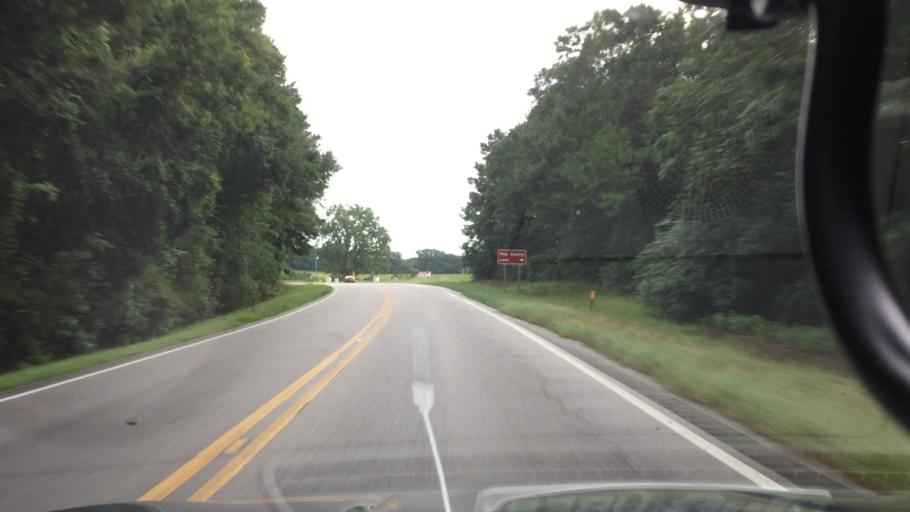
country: US
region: Alabama
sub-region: Pike County
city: Troy
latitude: 31.7477
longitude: -85.9595
